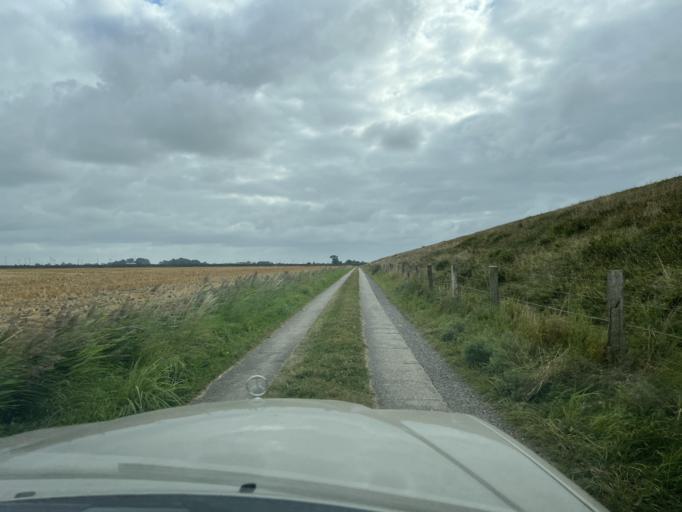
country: DE
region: Schleswig-Holstein
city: Lehe
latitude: 54.3308
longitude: 8.9932
